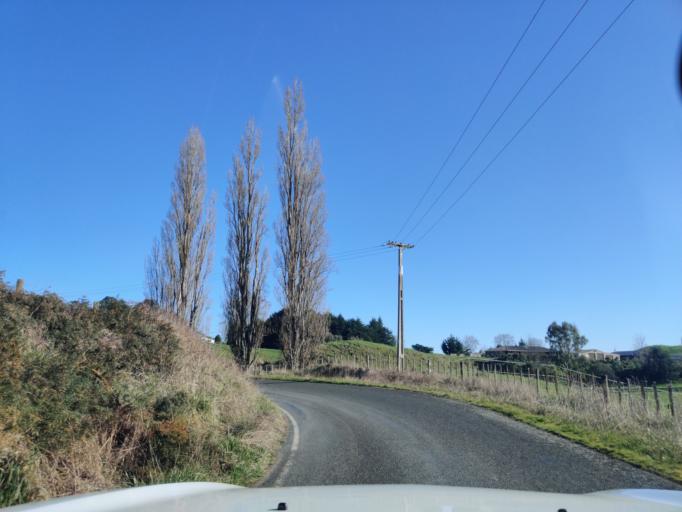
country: NZ
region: Waikato
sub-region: Matamata-Piako District
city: Matamata
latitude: -37.9936
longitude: 175.7188
